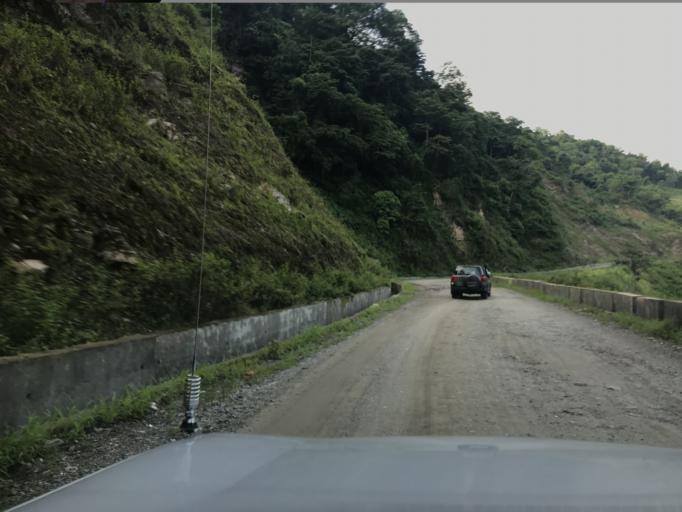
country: TL
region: Dili
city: Dili
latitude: -8.6353
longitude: 125.5145
